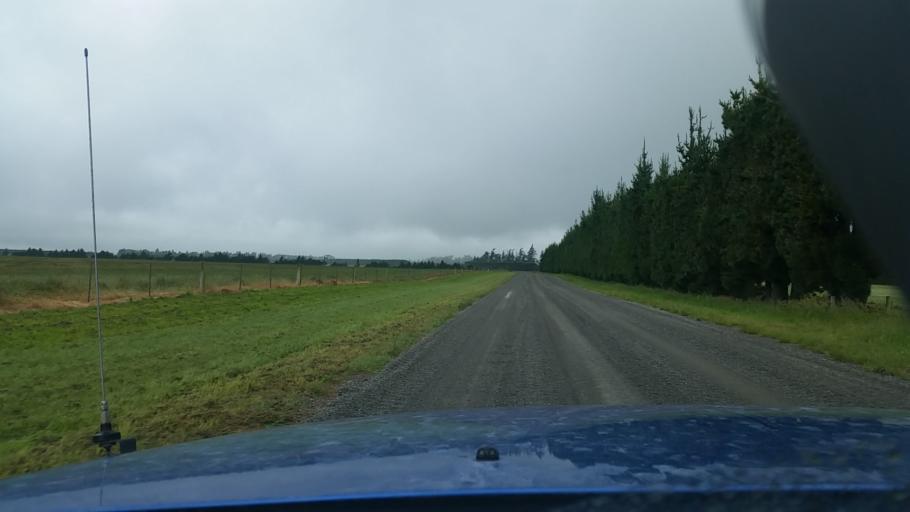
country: NZ
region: Canterbury
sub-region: Ashburton District
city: Methven
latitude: -43.6607
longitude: 171.8014
